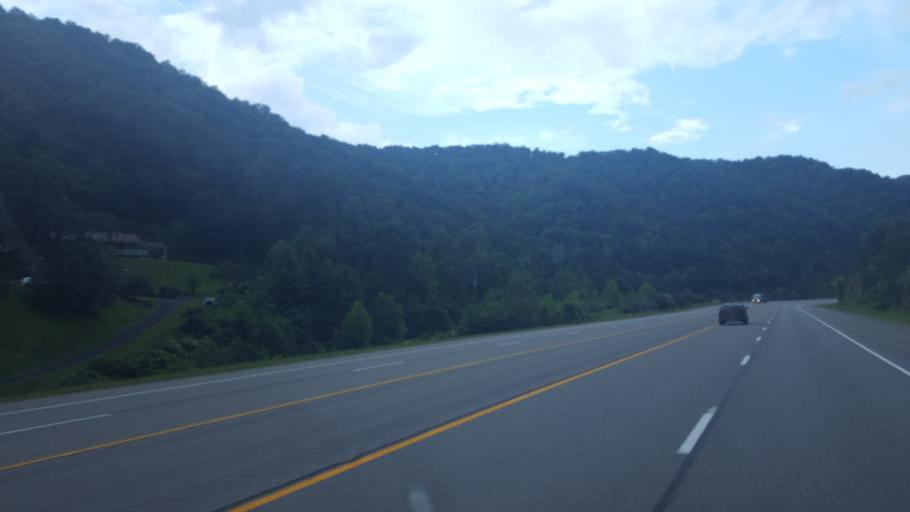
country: US
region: Kentucky
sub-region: Letcher County
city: Jenkins
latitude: 37.2633
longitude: -82.6130
